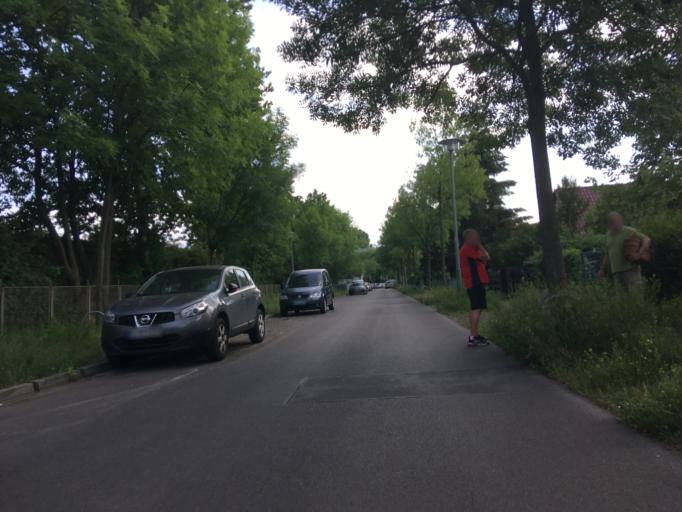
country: DE
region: Berlin
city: Adlershof
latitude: 52.4447
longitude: 13.5526
